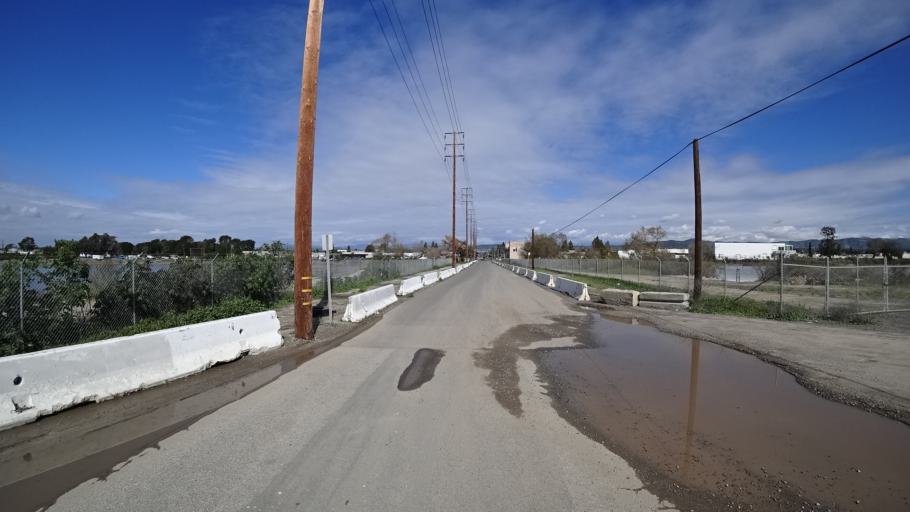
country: US
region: California
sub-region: Orange County
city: Yorba Linda
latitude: 33.8557
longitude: -117.8260
